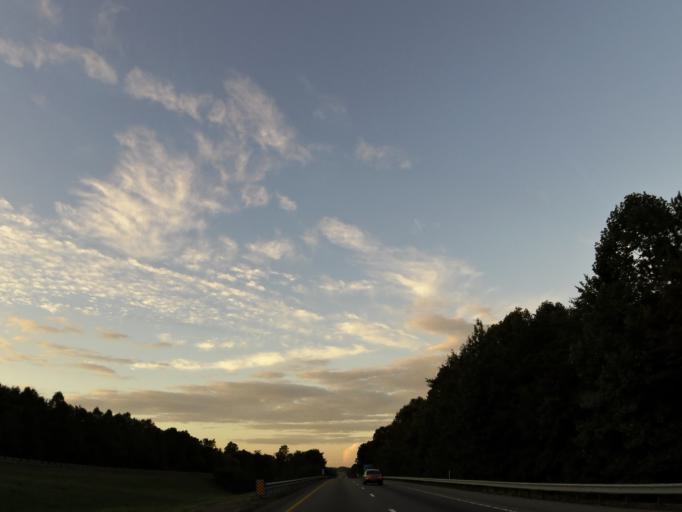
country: US
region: Tennessee
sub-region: McMinn County
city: Athens
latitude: 35.5289
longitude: -84.5855
